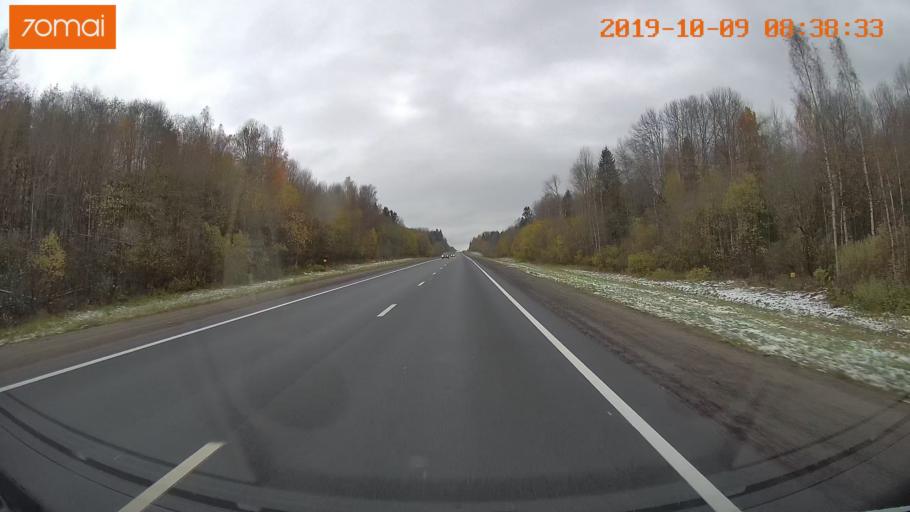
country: RU
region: Vologda
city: Gryazovets
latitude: 58.9582
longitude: 40.1643
